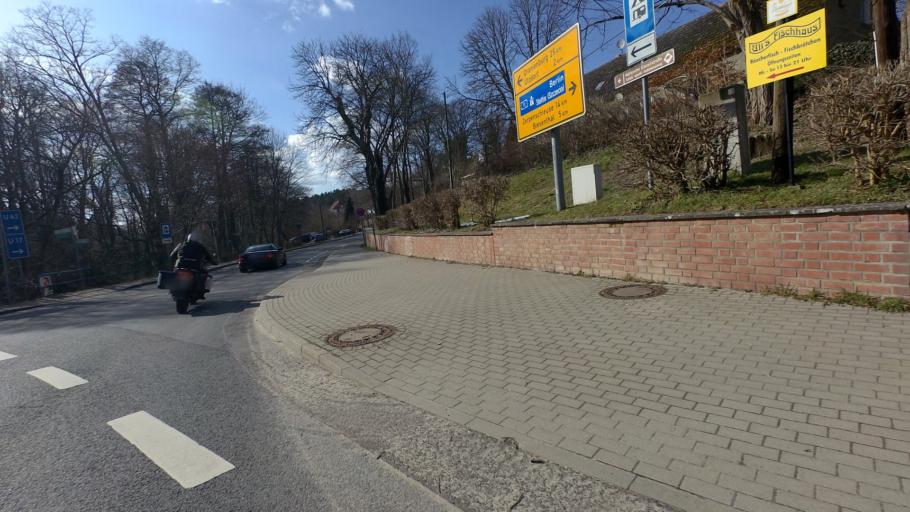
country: DE
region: Brandenburg
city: Rudnitz
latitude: 52.7608
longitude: 13.5634
